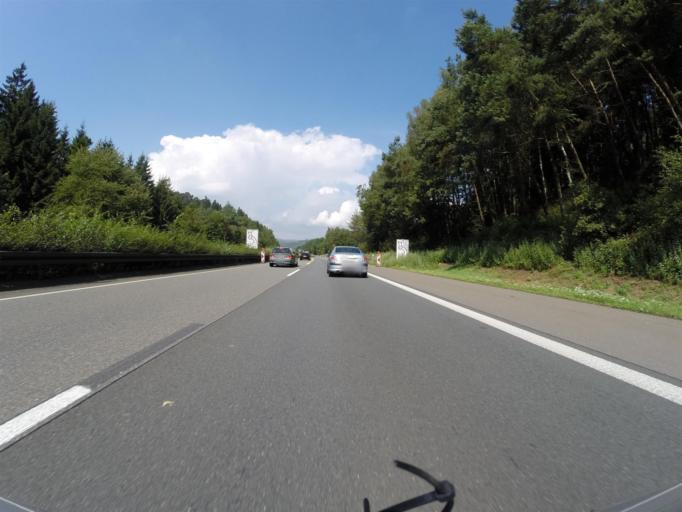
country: DE
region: Hesse
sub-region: Regierungsbezirk Kassel
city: Bad Arolsen
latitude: 51.5016
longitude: 8.9797
